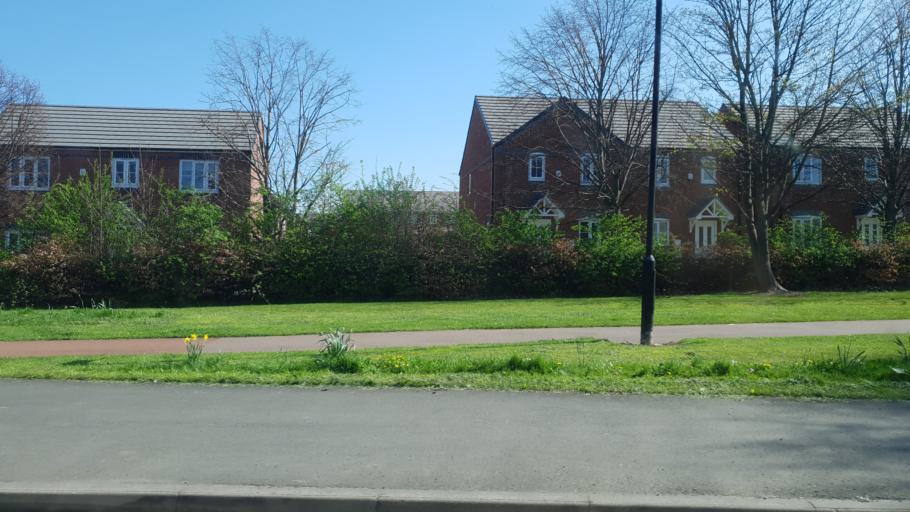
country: GB
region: England
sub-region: Middlesbrough
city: Middlesbrough
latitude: 54.5473
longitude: -1.2159
